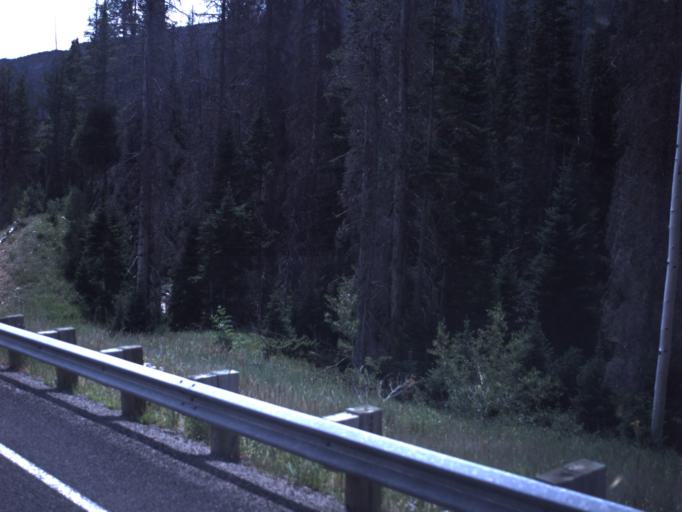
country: US
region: Utah
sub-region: Summit County
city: Francis
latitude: 40.4809
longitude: -110.9433
